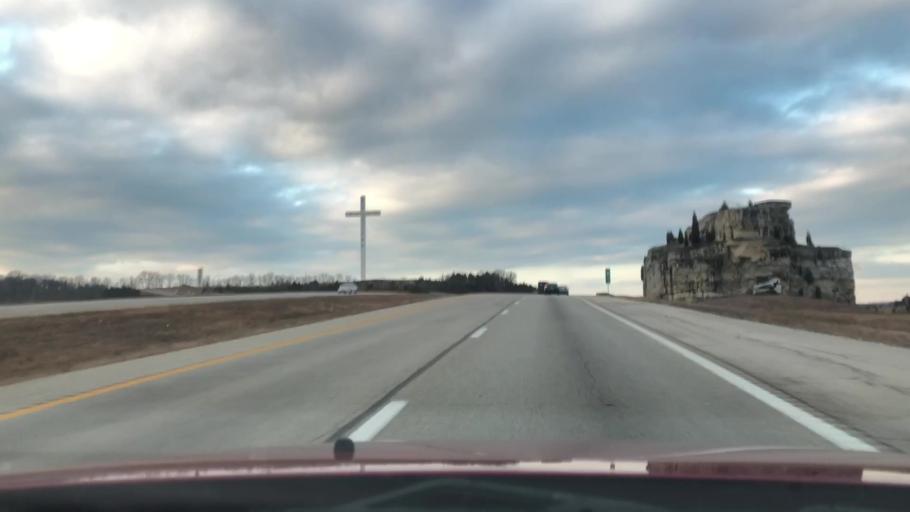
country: US
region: Missouri
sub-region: Taney County
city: Merriam Woods
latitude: 36.7464
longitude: -93.2225
